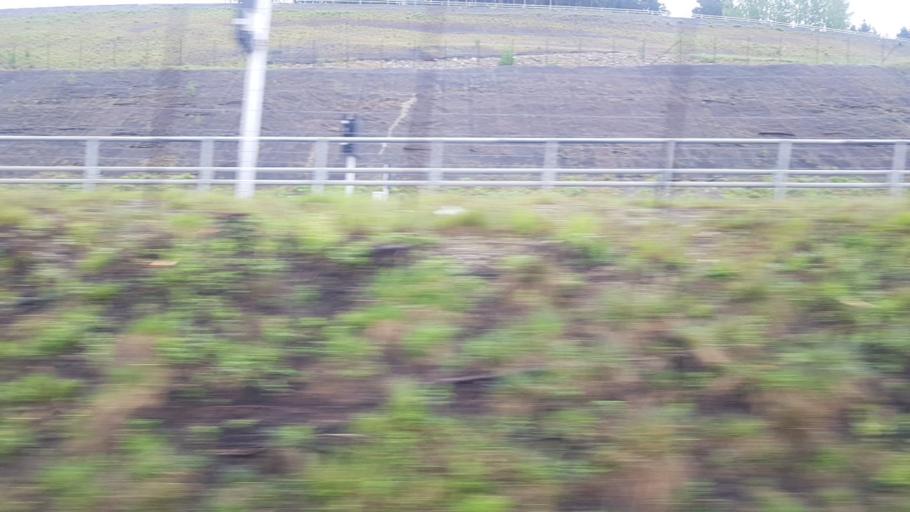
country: NO
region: Oppland
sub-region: Sor-Fron
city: Hundorp
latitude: 61.5587
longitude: 9.9348
